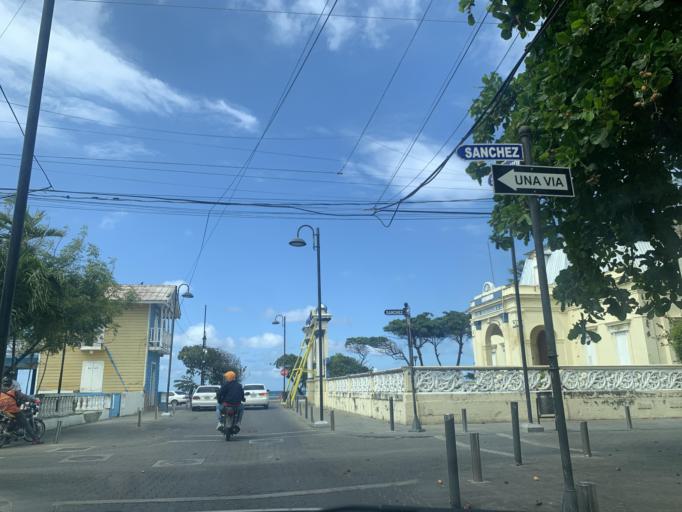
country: DO
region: Puerto Plata
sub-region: Puerto Plata
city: Puerto Plata
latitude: 19.7995
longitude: -70.6916
